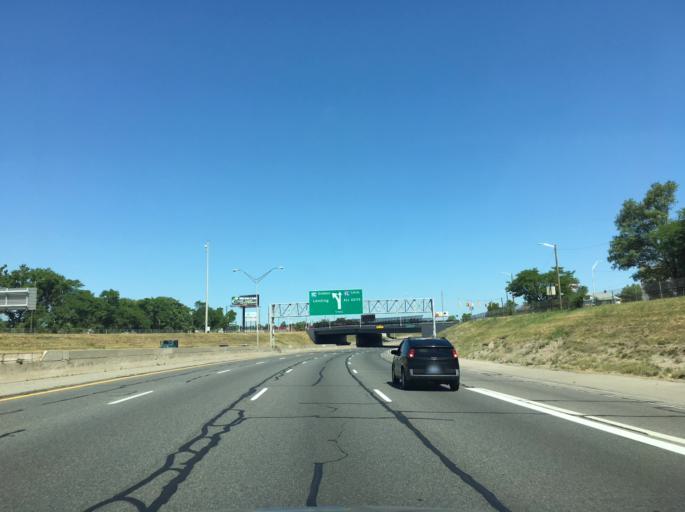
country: US
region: Michigan
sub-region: Wayne County
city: Dearborn
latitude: 42.3695
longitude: -83.1433
